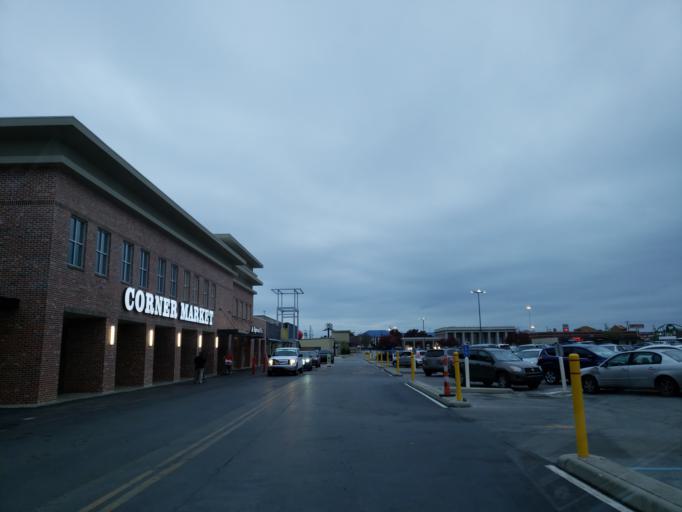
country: US
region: Mississippi
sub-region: Lamar County
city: West Hattiesburg
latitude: 31.3234
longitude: -89.3448
